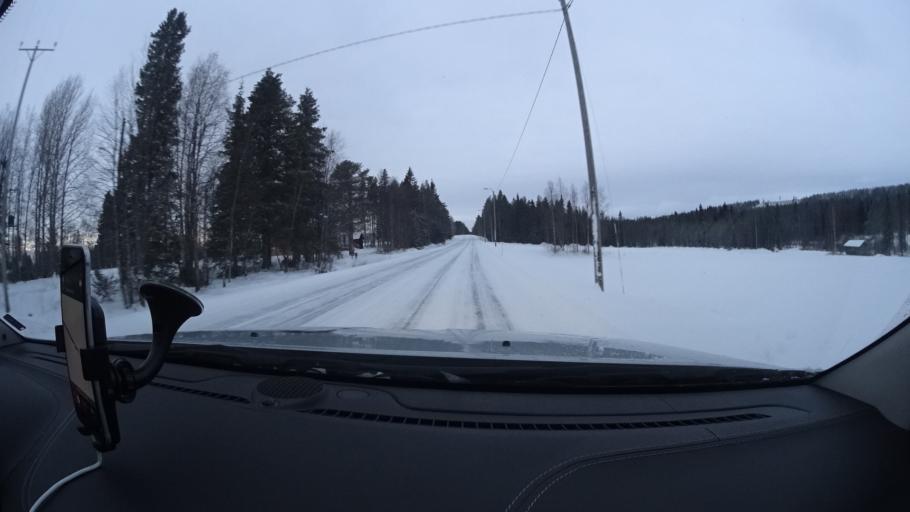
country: FI
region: Northern Ostrobothnia
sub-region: Koillismaa
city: Kuusamo
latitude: 66.0969
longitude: 28.6945
